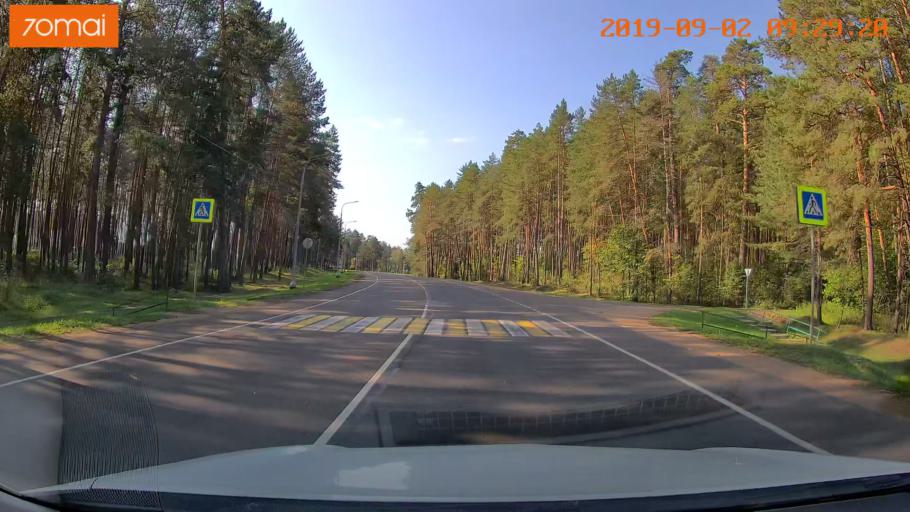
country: RU
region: Kaluga
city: Yukhnov
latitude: 54.7422
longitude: 35.2148
